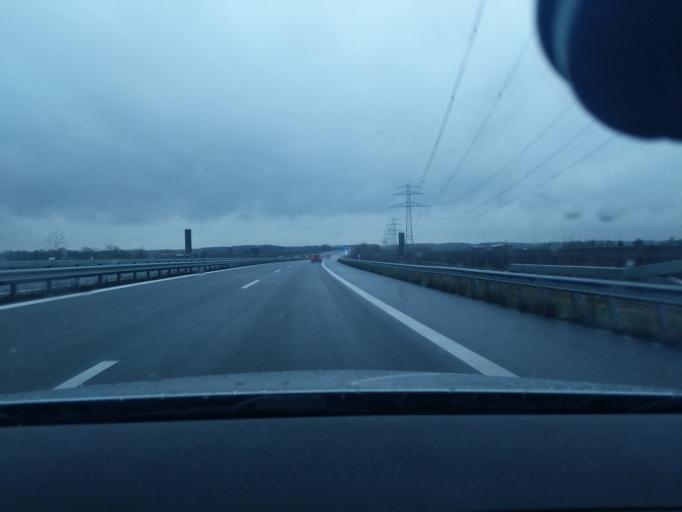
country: DE
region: Lower Saxony
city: Neuenkirchen
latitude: 53.5119
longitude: 9.6077
